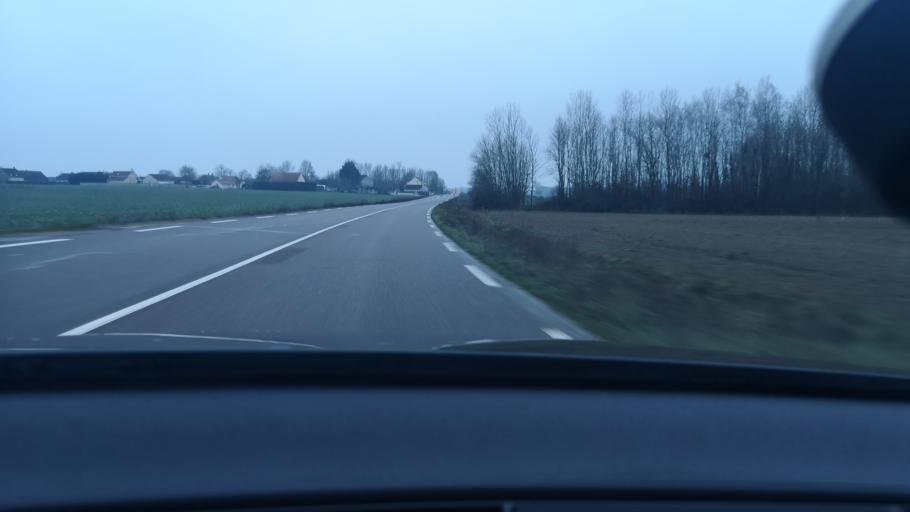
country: FR
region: Bourgogne
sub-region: Departement de la Cote-d'Or
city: Seurre
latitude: 47.0877
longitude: 5.1068
